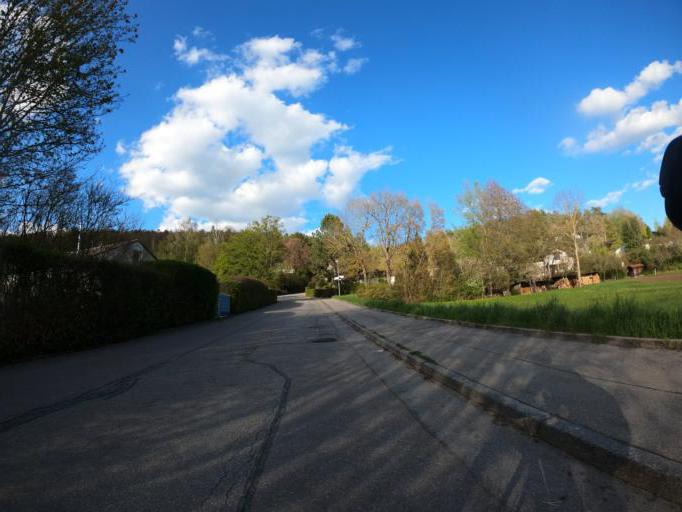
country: DE
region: Baden-Wuerttemberg
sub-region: Regierungsbezirk Stuttgart
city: Aidlingen
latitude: 48.6819
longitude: 8.9078
